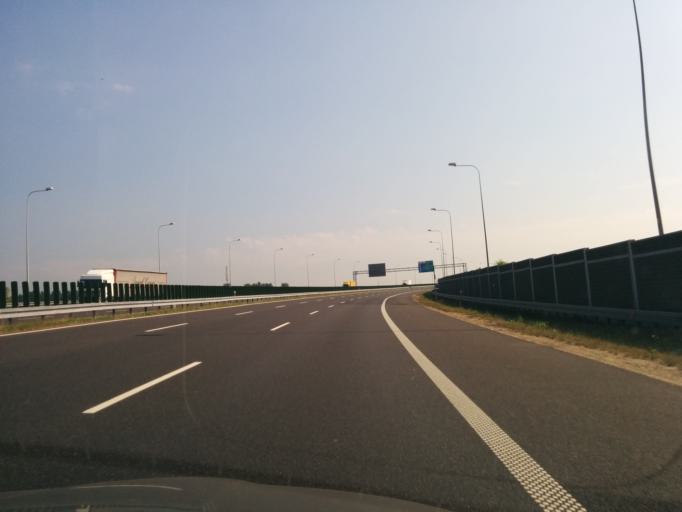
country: PL
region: Silesian Voivodeship
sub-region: Gliwice
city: Gliwice
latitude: 50.2920
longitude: 18.7157
